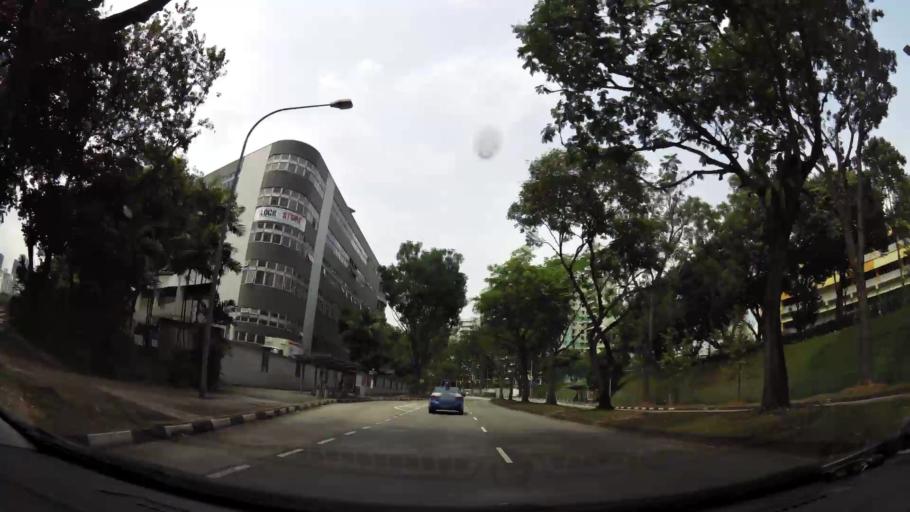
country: SG
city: Singapore
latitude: 1.3447
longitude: 103.7524
